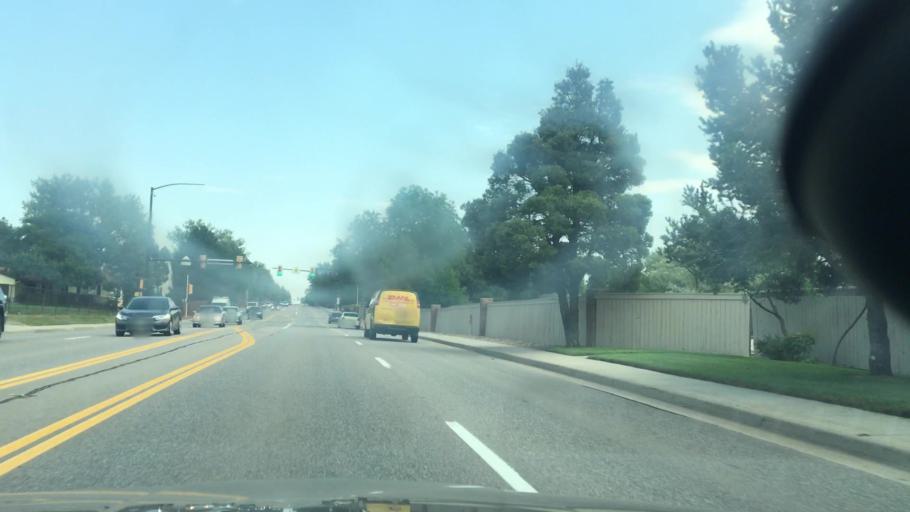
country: US
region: Colorado
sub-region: Arapahoe County
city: Castlewood
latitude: 39.5805
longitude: -104.8989
